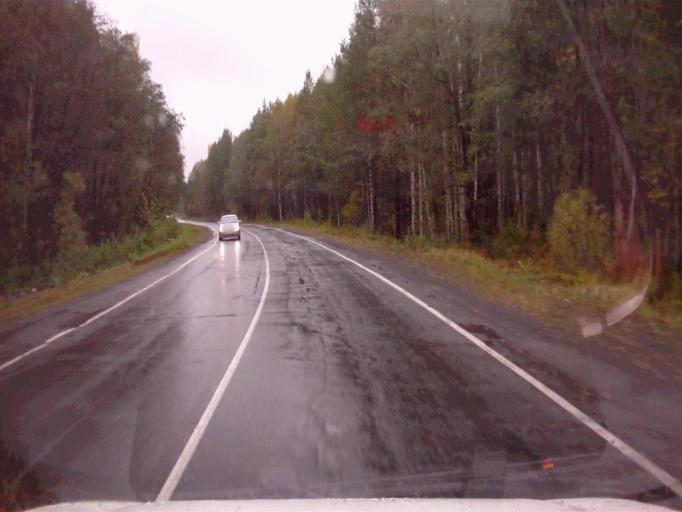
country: RU
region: Chelyabinsk
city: Verkhniy Ufaley
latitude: 55.9582
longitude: 60.3891
